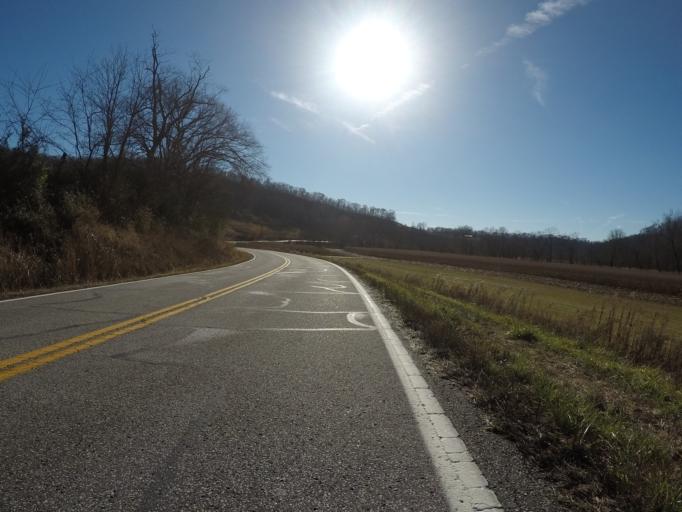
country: US
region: West Virginia
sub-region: Cabell County
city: Huntington
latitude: 38.4784
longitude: -82.4456
